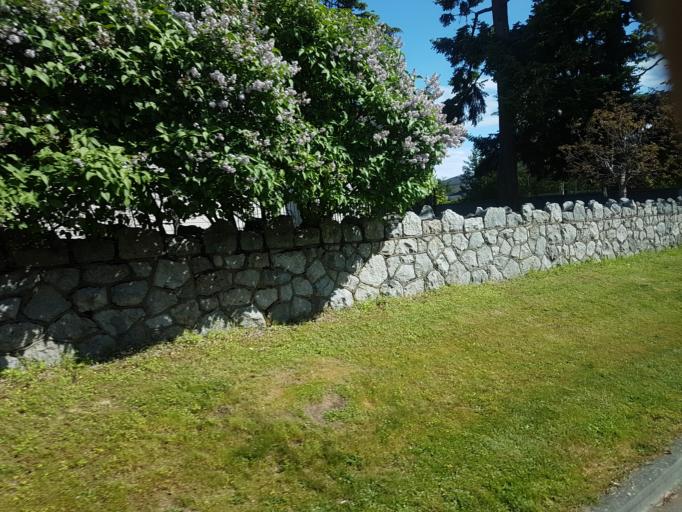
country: CA
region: British Columbia
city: Oak Bay
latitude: 48.4868
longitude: -123.3194
